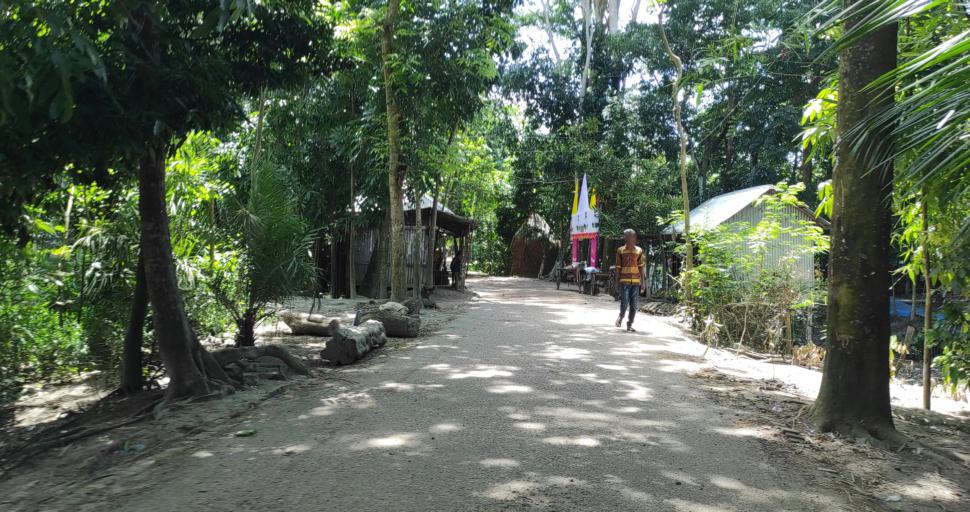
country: BD
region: Barisal
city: Gaurnadi
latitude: 22.9184
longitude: 90.0797
